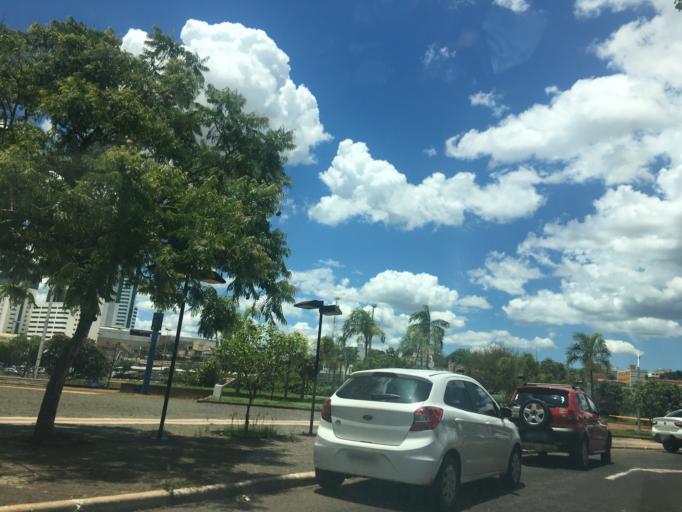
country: BR
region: Minas Gerais
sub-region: Uberlandia
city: Uberlandia
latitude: -18.9130
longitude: -48.2575
